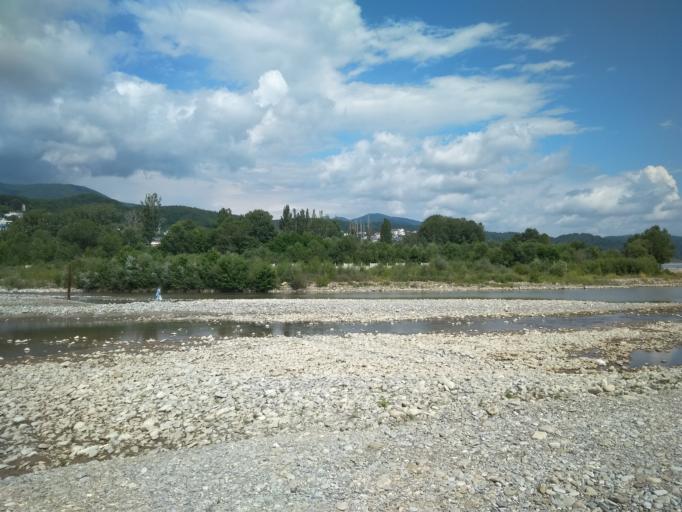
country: RU
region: Krasnodarskiy
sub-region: Sochi City
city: Lazarevskoye
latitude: 43.8990
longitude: 39.3333
